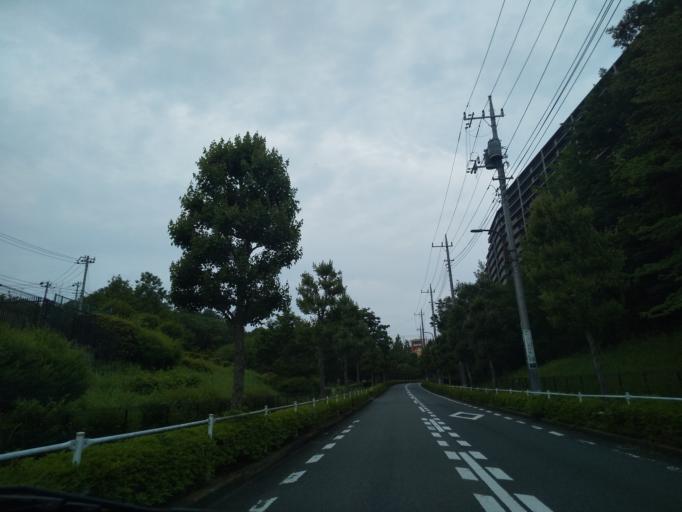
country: JP
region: Tokyo
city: Hachioji
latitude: 35.6015
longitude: 139.3613
